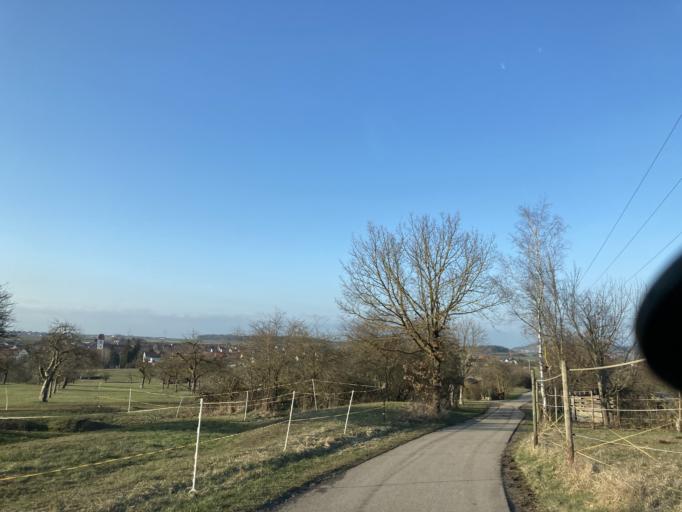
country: DE
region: Baden-Wuerttemberg
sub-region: Tuebingen Region
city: Hirrlingen
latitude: 48.4032
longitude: 8.8920
